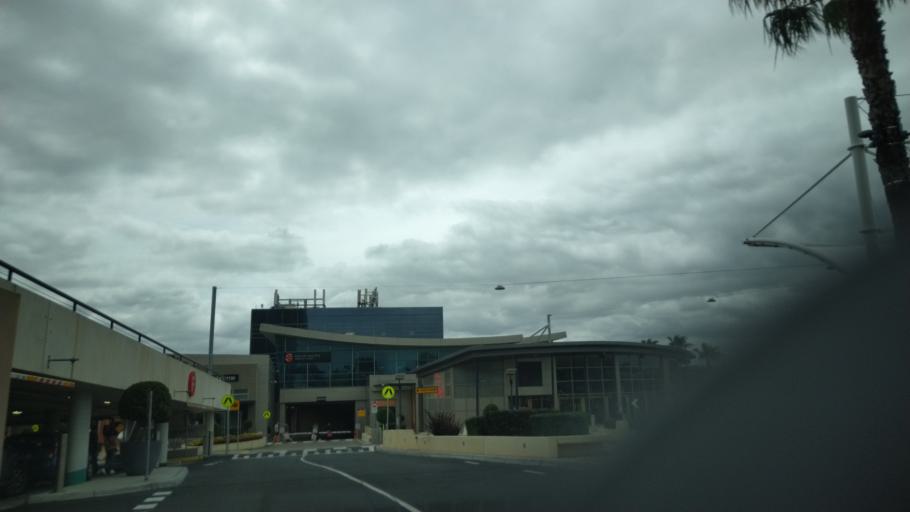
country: AU
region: Victoria
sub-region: Monash
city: Chadstone
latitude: -37.8878
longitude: 145.0832
